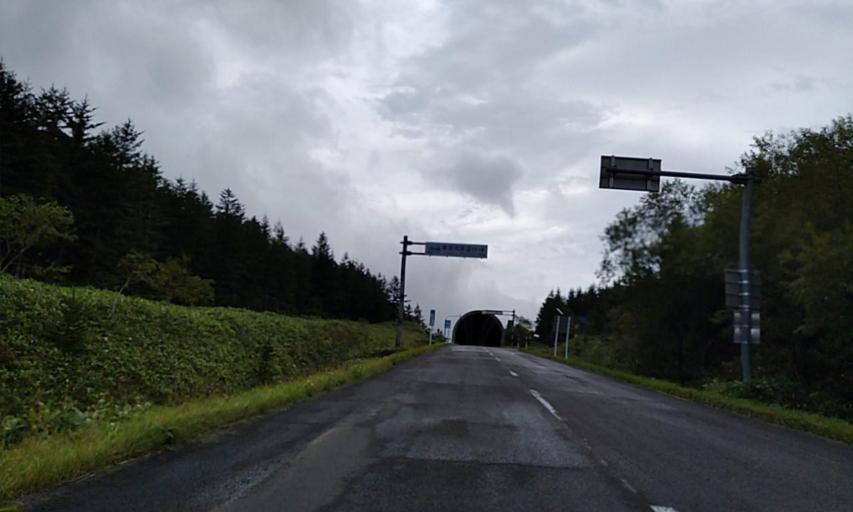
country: JP
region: Hokkaido
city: Abashiri
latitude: 43.6137
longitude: 144.5902
